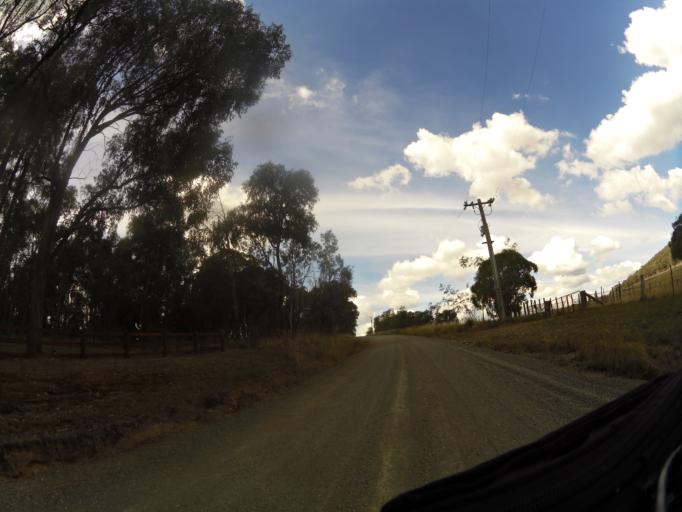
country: AU
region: Victoria
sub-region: Benalla
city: Benalla
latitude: -36.7808
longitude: 145.9815
